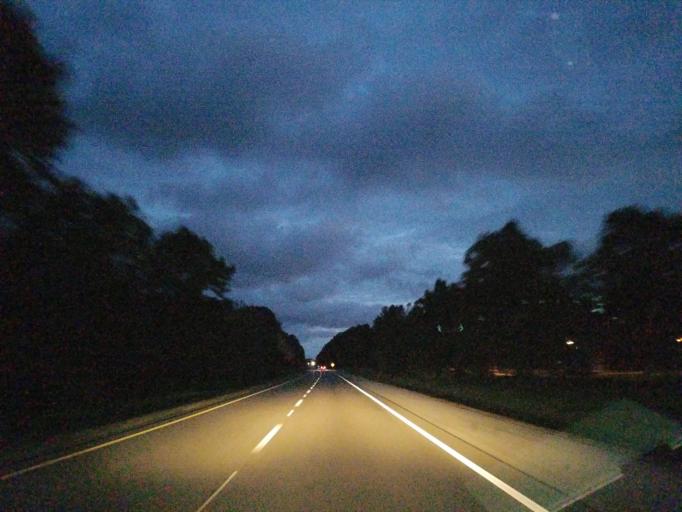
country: US
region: Mississippi
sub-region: Jones County
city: Sharon
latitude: 31.8521
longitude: -89.0489
